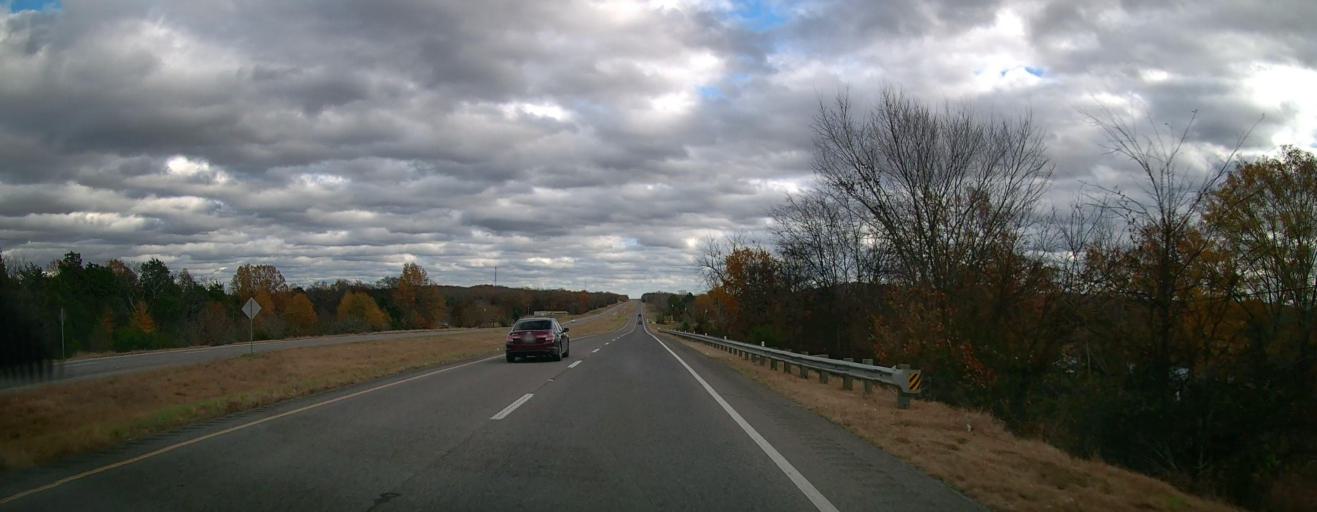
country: US
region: Alabama
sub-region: Morgan County
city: Danville
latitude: 34.4132
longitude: -87.1554
